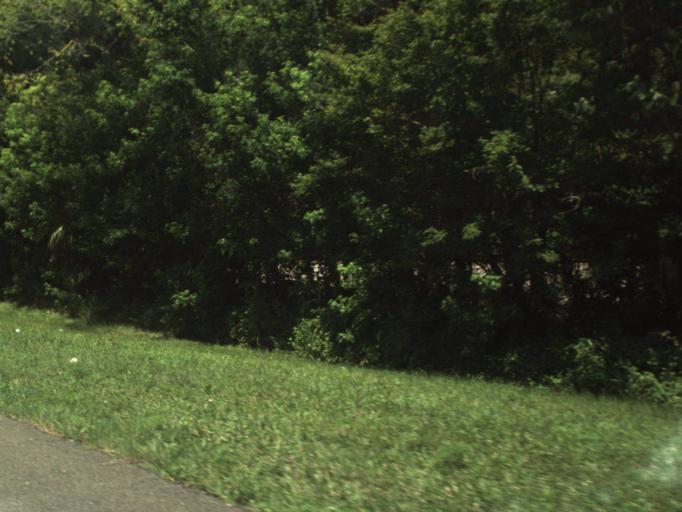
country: US
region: Florida
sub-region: Seminole County
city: Winter Springs
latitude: 28.7145
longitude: -81.3076
